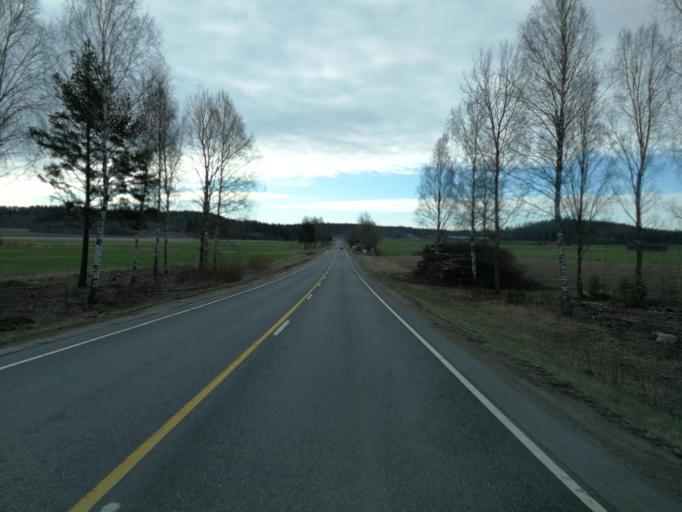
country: FI
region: Varsinais-Suomi
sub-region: Salo
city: Muurla
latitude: 60.3797
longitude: 23.2994
